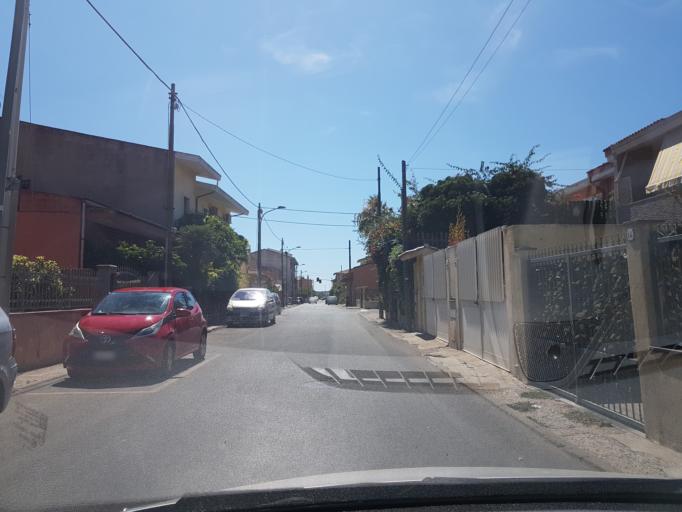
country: IT
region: Sardinia
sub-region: Provincia di Oristano
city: Cabras
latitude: 39.9247
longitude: 8.5349
